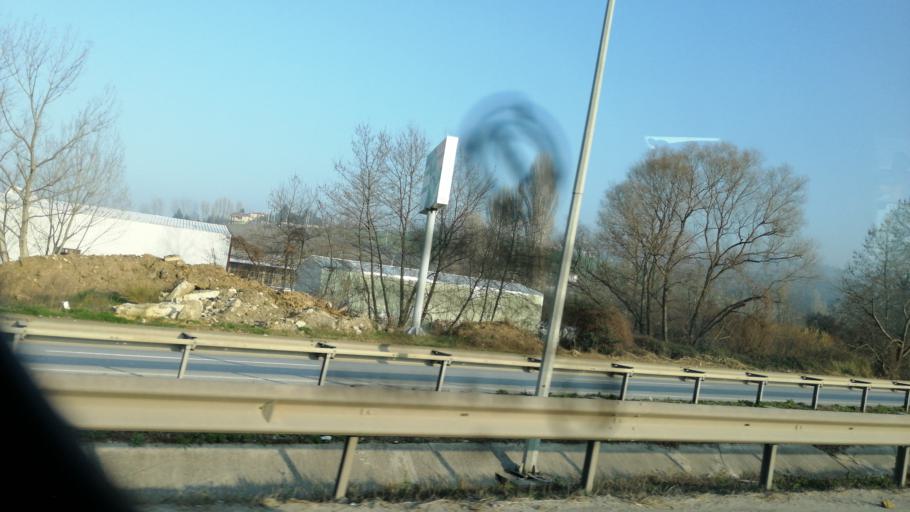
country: TR
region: Yalova
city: Yalova
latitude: 40.6223
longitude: 29.2707
